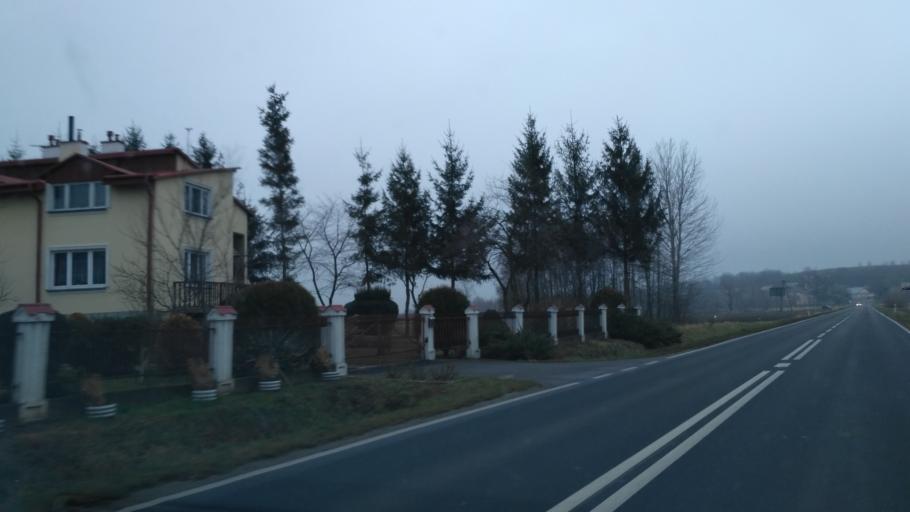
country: PL
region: Subcarpathian Voivodeship
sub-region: Powiat jaroslawski
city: Pruchnik
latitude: 49.9244
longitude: 22.5692
